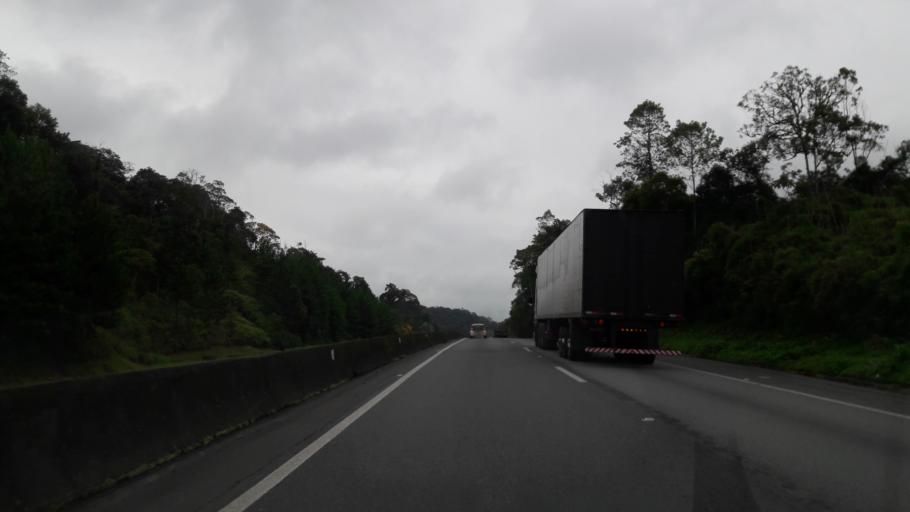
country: BR
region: Sao Paulo
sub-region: Cajati
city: Cajati
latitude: -24.9711
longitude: -48.3716
